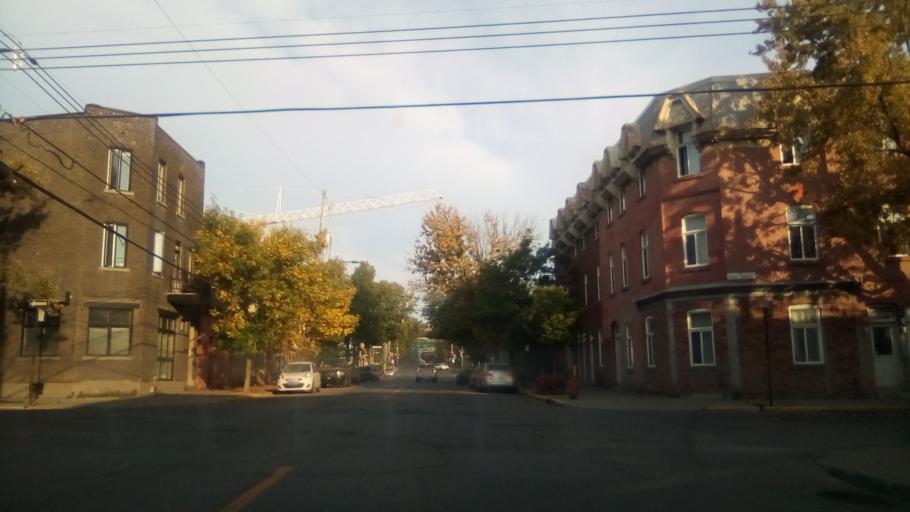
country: CA
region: Quebec
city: Westmount
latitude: 45.4789
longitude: -73.5700
